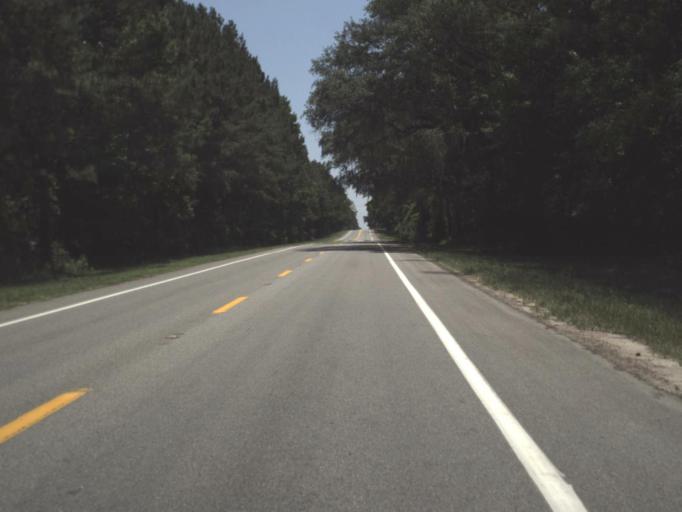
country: US
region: Florida
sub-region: Suwannee County
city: Live Oak
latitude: 30.3643
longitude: -83.1362
